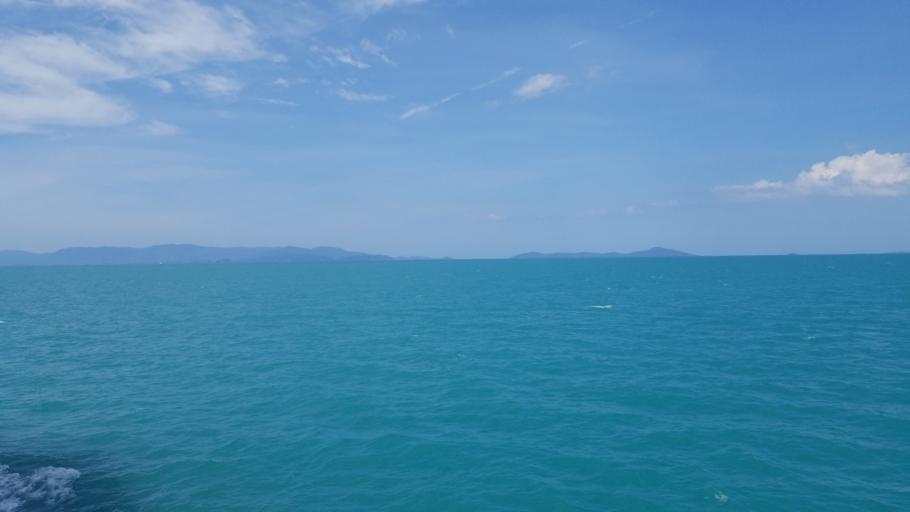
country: TH
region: Surat Thani
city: Don Sak
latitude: 9.3853
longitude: 99.7896
